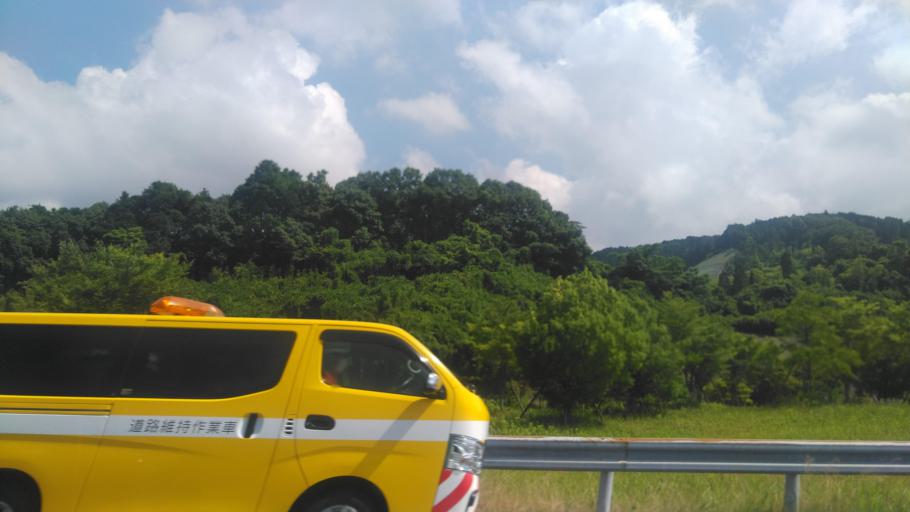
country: JP
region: Fukuoka
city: Tanushimarumachi-toyoki
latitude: 33.3698
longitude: 130.8075
